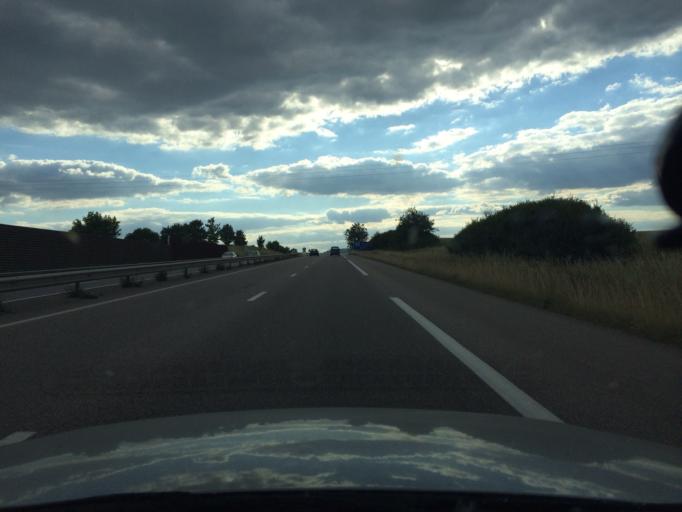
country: FR
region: Lorraine
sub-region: Departement de Meurthe-et-Moselle
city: Art-sur-Meurthe
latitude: 48.6186
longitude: 6.2505
